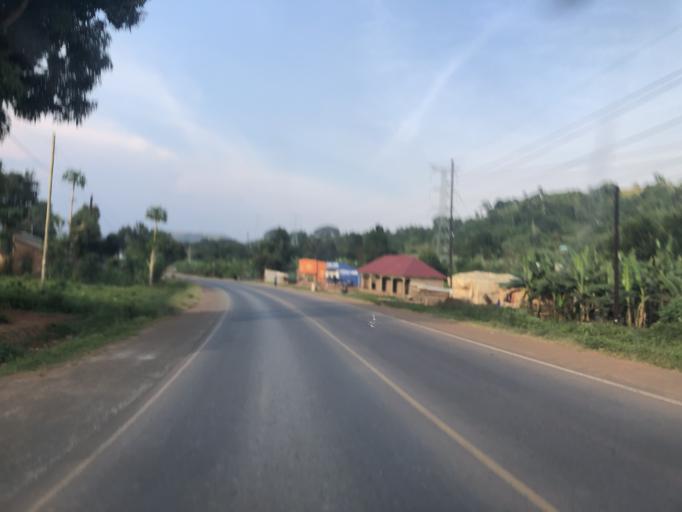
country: UG
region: Central Region
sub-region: Mpigi District
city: Mpigi
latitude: 0.1736
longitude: 32.2733
